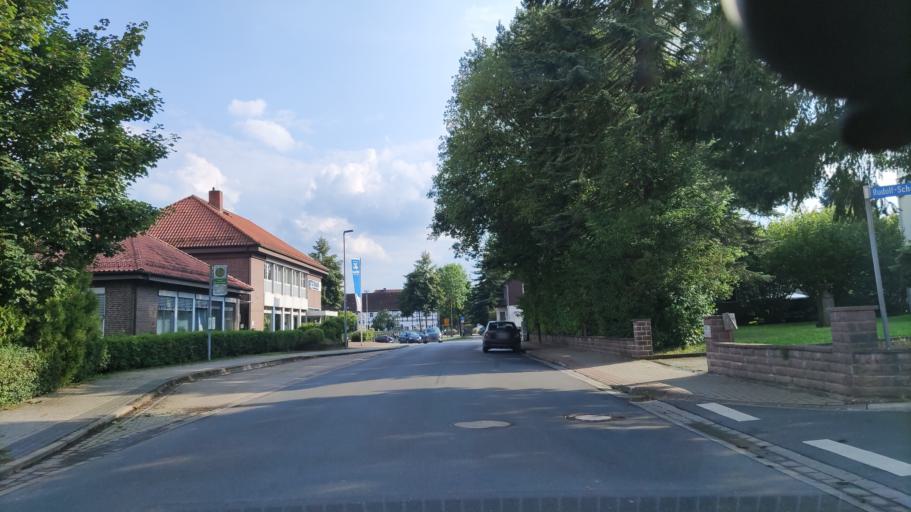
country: DE
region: Lower Saxony
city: Dassel
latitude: 51.8040
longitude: 9.6876
